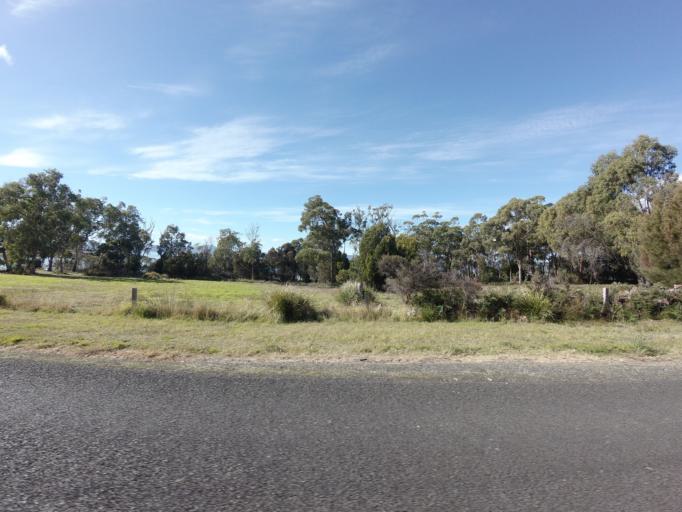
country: AU
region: Tasmania
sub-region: Clarence
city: Sandford
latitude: -42.9989
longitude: 147.7087
